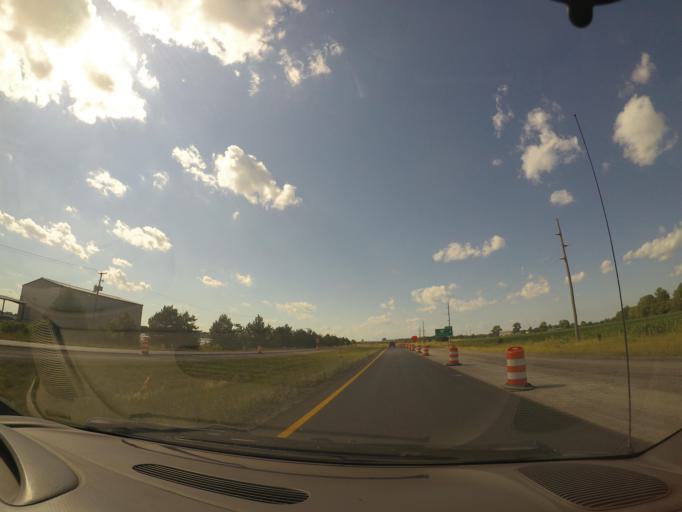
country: US
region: Ohio
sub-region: Sandusky County
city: Fremont
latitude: 41.3513
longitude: -83.0728
